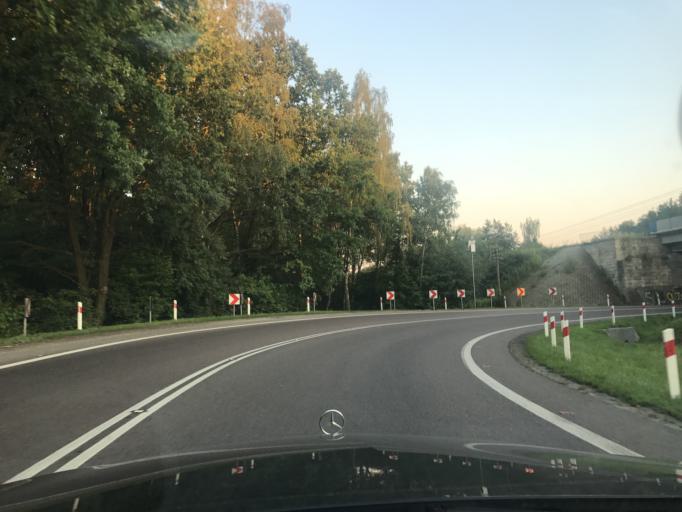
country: PL
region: Lublin Voivodeship
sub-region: Powiat lubelski
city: Niemce
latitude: 51.3870
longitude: 22.6360
